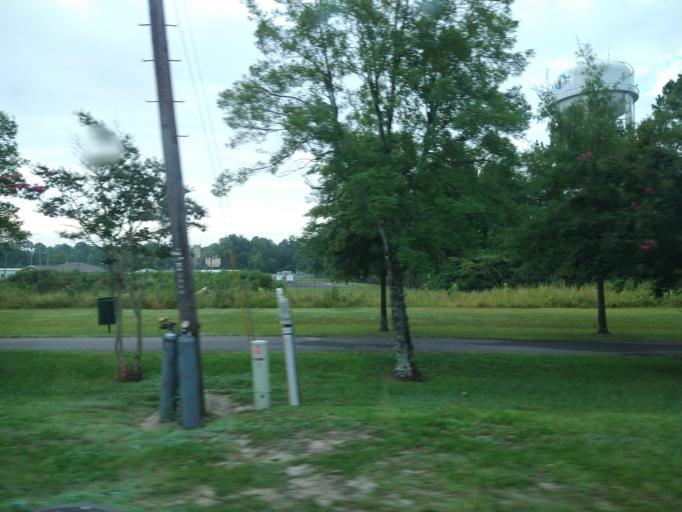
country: US
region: North Carolina
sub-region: Onslow County
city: Jacksonville
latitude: 34.7645
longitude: -77.4105
